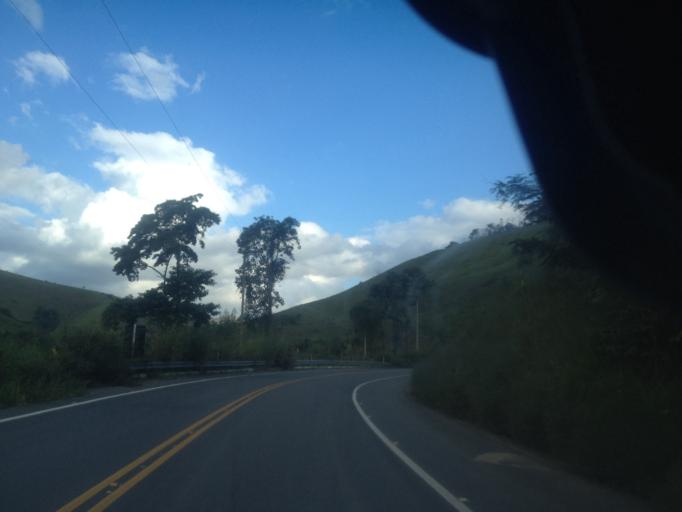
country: BR
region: Rio de Janeiro
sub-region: Quatis
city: Quatis
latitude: -22.2663
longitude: -44.2616
